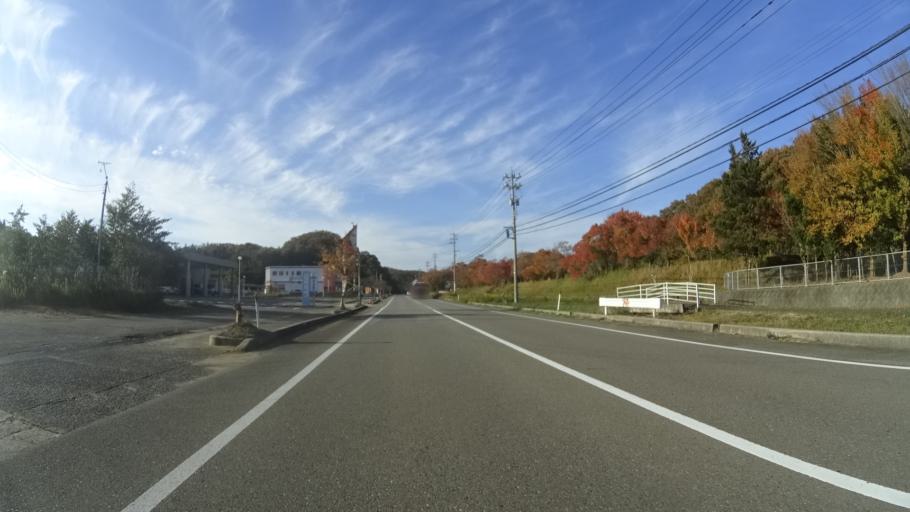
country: JP
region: Ishikawa
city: Hakui
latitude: 37.0258
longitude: 136.7836
